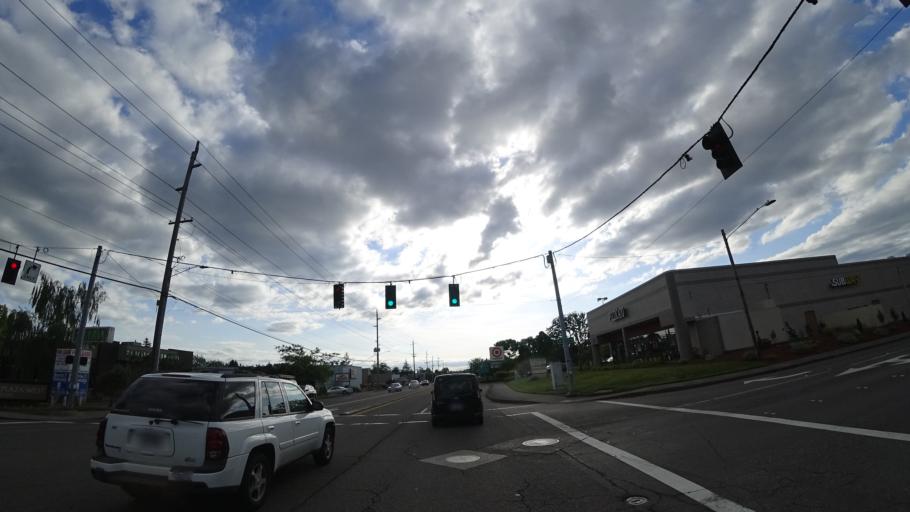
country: US
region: Oregon
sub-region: Washington County
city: Beaverton
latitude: 45.4866
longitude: -122.7867
